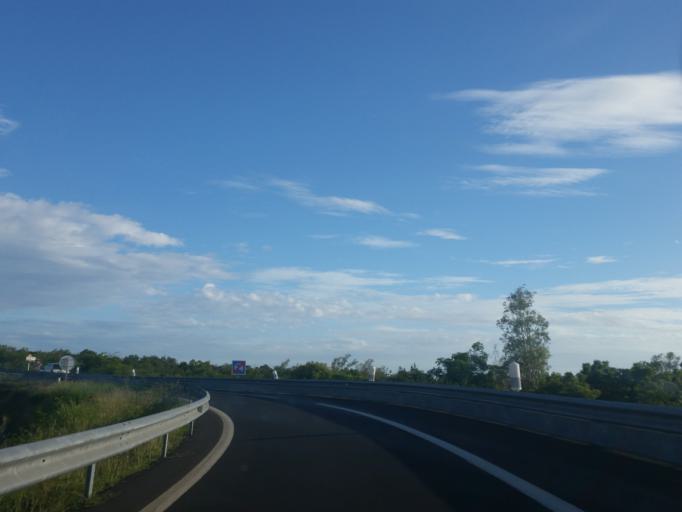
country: RE
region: Reunion
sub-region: Reunion
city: Les Avirons
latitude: -21.2632
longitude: 55.3377
